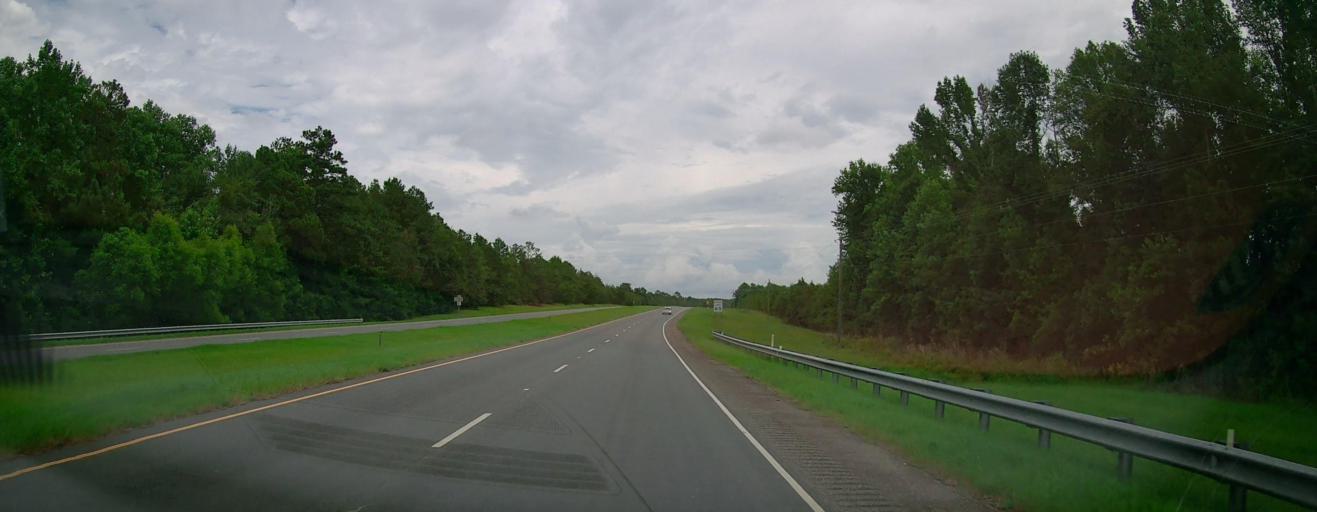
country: US
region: Georgia
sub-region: Telfair County
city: Helena
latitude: 32.1047
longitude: -82.9876
